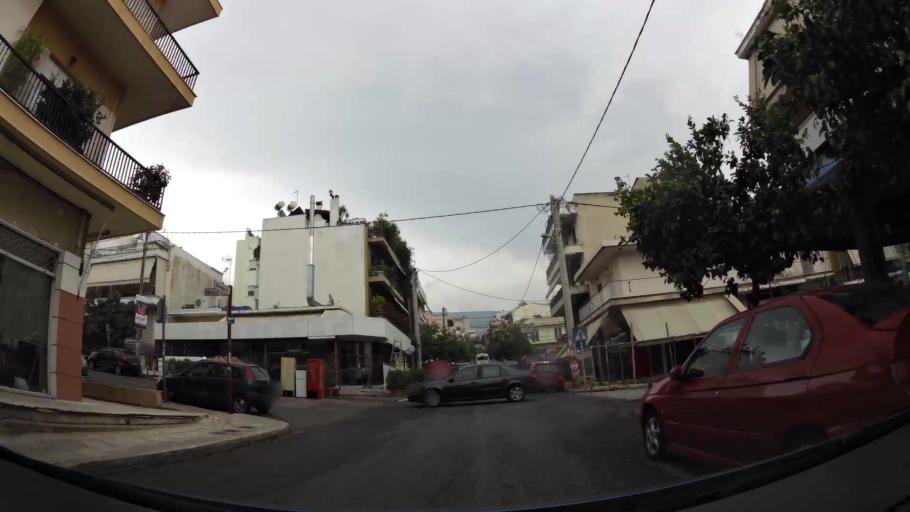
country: GR
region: Attica
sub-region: Nomarchia Athinas
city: Kaisariani
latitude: 37.9558
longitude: 23.7647
